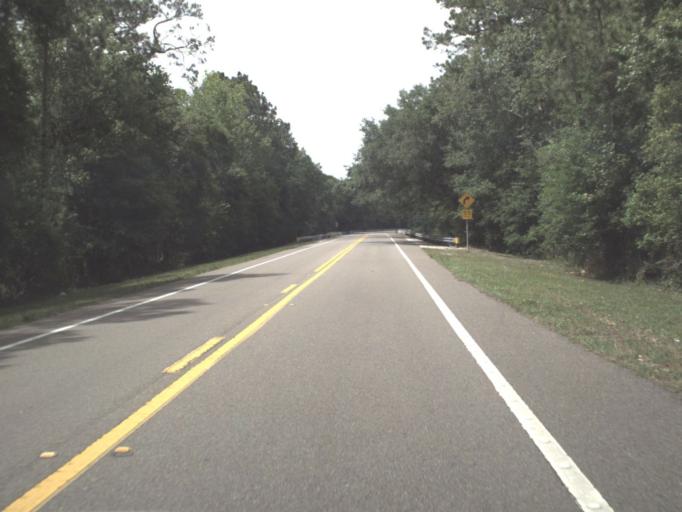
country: US
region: Florida
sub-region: Volusia County
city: Pierson
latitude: 29.2670
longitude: -81.3354
